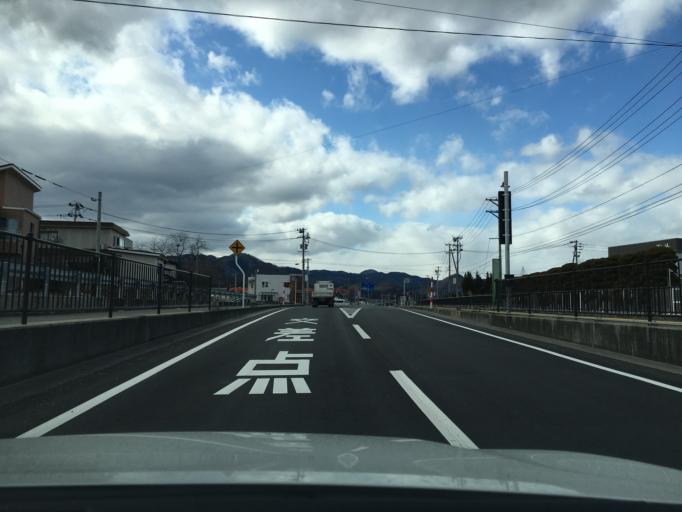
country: JP
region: Yamagata
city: Kaminoyama
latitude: 38.2085
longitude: 140.3027
